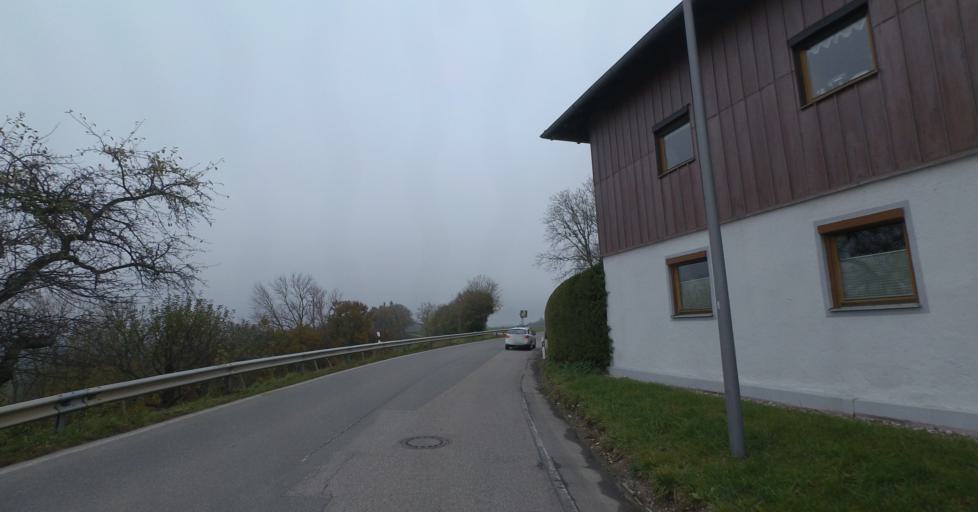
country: DE
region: Bavaria
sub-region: Upper Bavaria
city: Trostberg an der Alz
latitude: 47.9794
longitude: 12.5261
